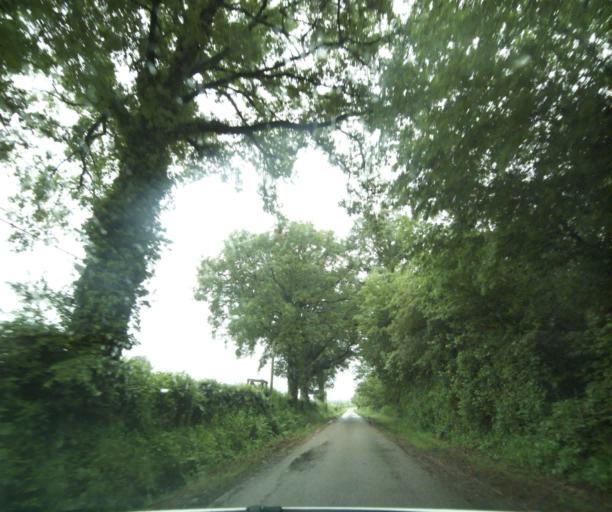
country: FR
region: Bourgogne
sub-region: Departement de Saone-et-Loire
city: Charolles
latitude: 46.4655
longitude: 4.2181
